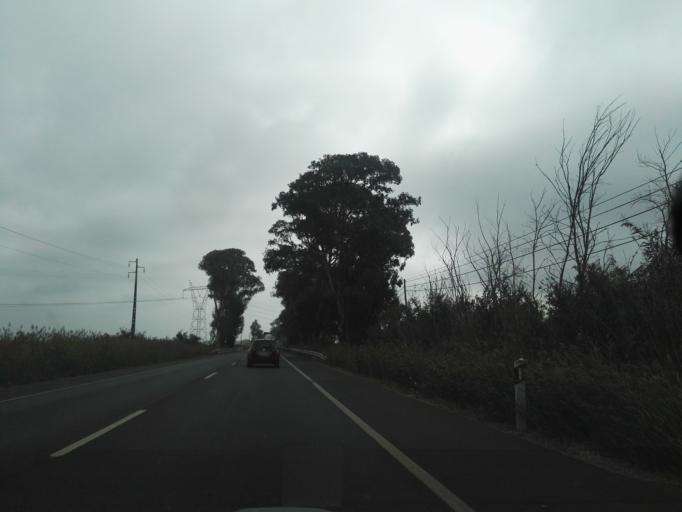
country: PT
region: Lisbon
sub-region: Vila Franca de Xira
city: Vila Franca de Xira
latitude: 38.9457
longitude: -8.9562
